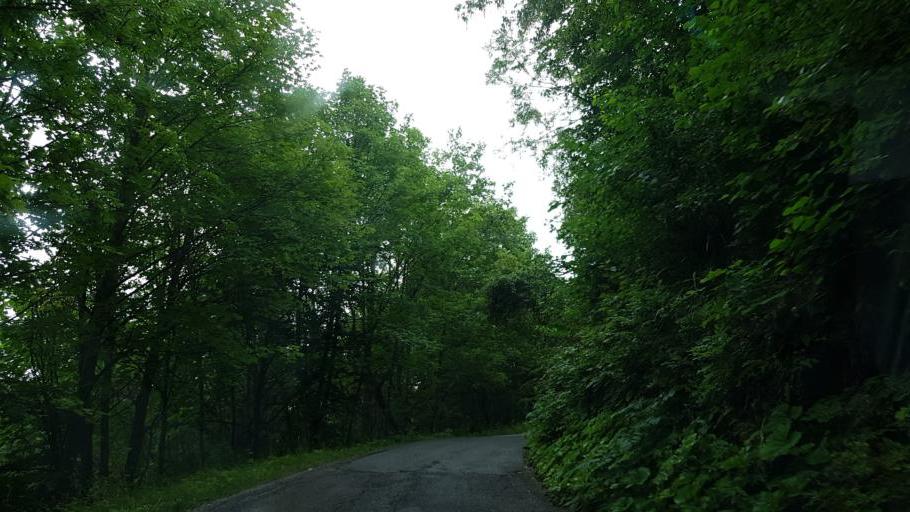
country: IT
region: Piedmont
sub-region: Provincia di Cuneo
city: Stroppo
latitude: 44.5151
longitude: 7.1148
